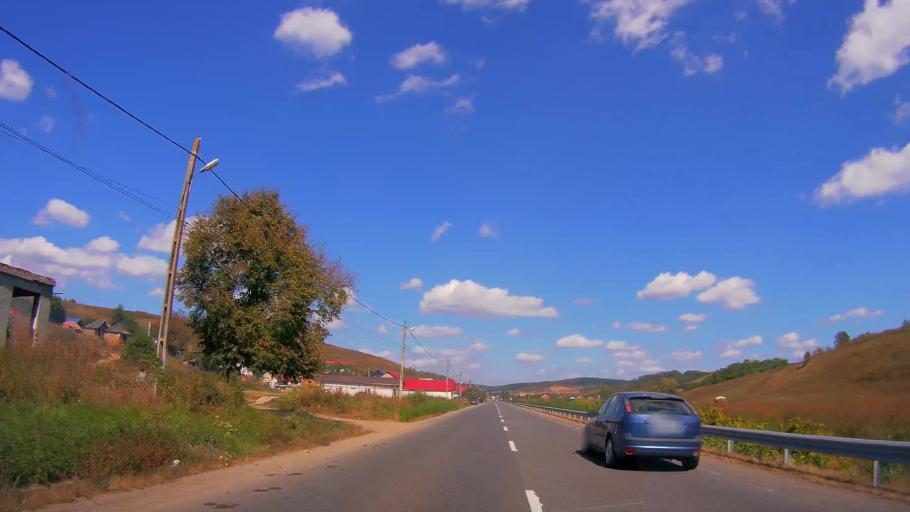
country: RO
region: Cluj
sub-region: Comuna Sanpaul
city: Sanpaul
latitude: 46.8632
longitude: 23.4097
